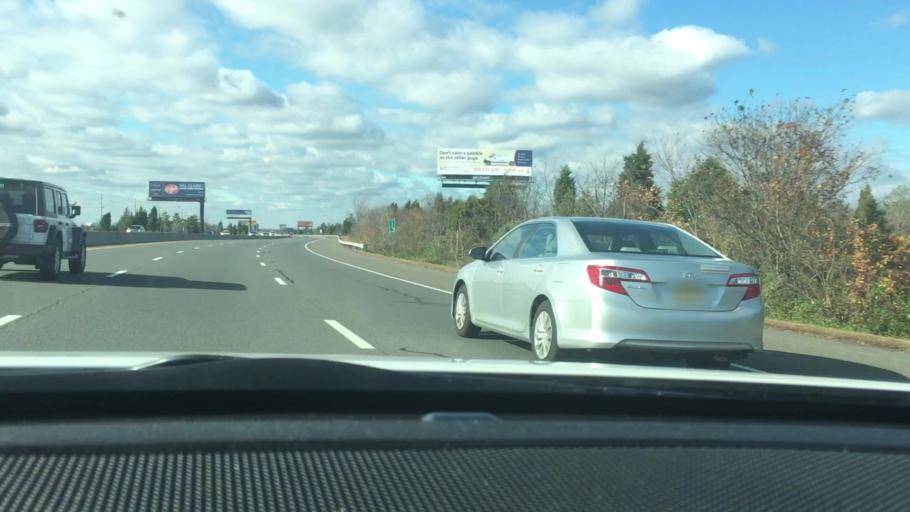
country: US
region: New Jersey
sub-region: Atlantic County
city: Ventnor City
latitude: 39.3682
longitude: -74.4628
